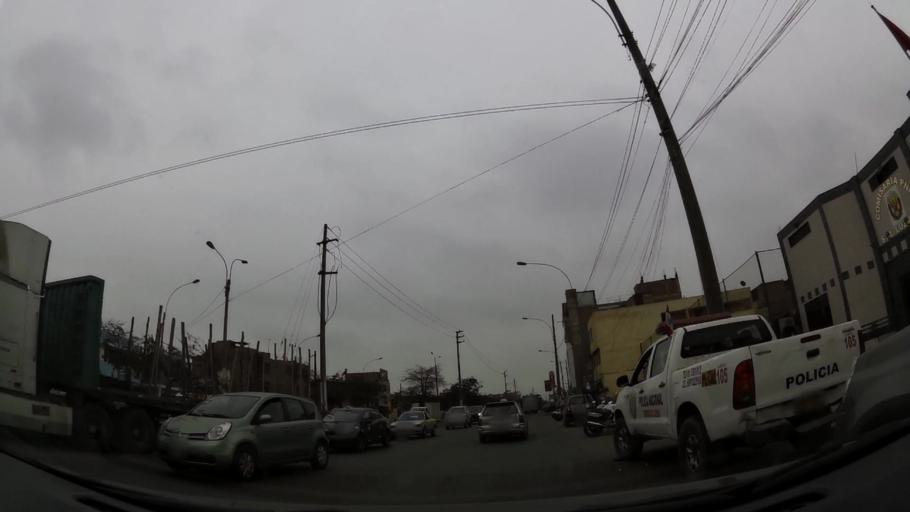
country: PE
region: Lima
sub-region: Lima
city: Independencia
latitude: -11.9446
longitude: -77.0665
